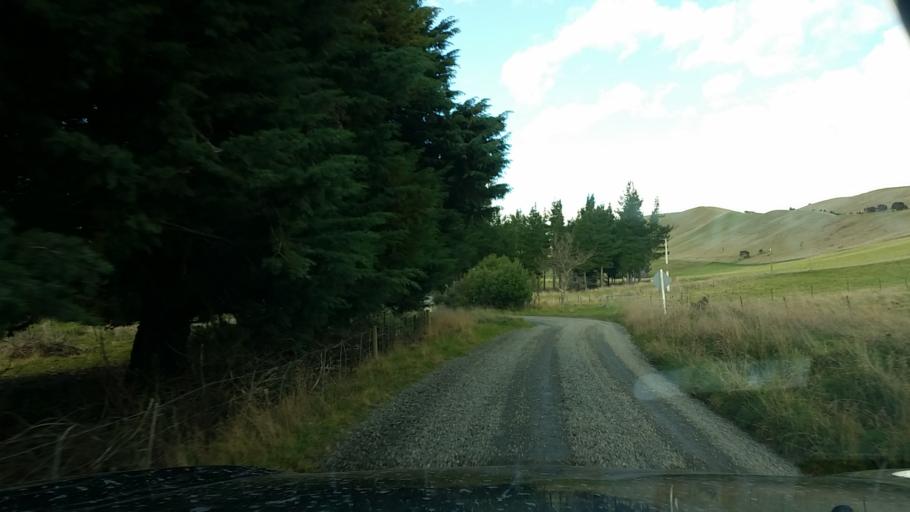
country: NZ
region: Marlborough
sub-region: Marlborough District
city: Blenheim
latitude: -41.7668
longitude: 173.8613
